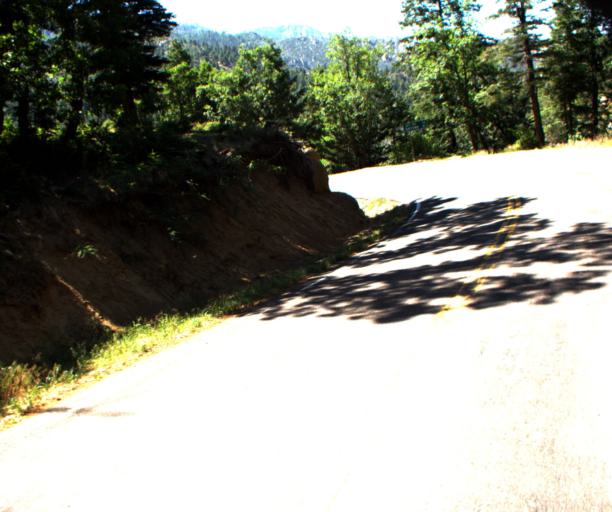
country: US
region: Arizona
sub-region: Graham County
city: Swift Trail Junction
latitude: 32.6351
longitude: -109.8186
